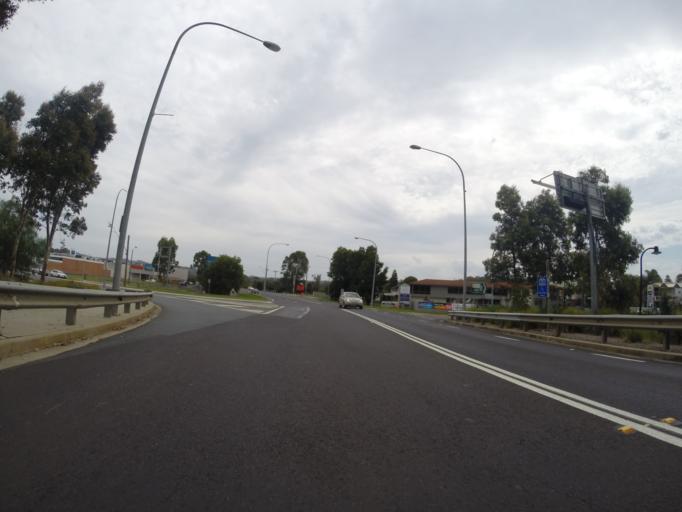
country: AU
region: New South Wales
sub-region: Eurobodalla
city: Batemans Bay
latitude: -35.7028
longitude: 150.1779
